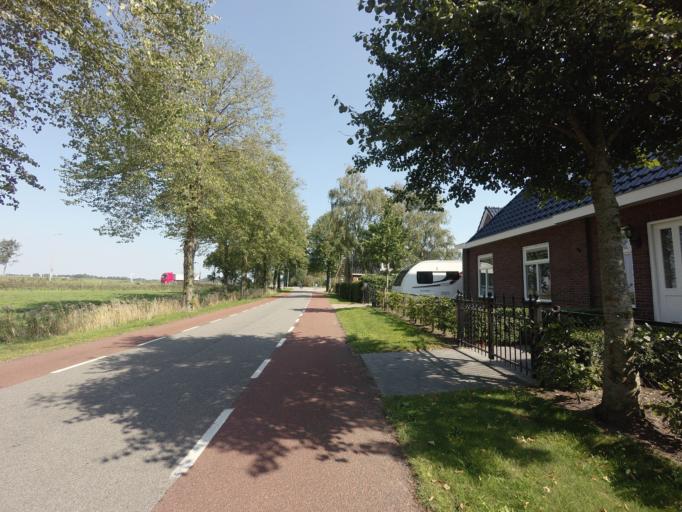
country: NL
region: Groningen
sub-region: Gemeente Zuidhorn
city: Grijpskerk
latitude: 53.2637
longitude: 6.3178
